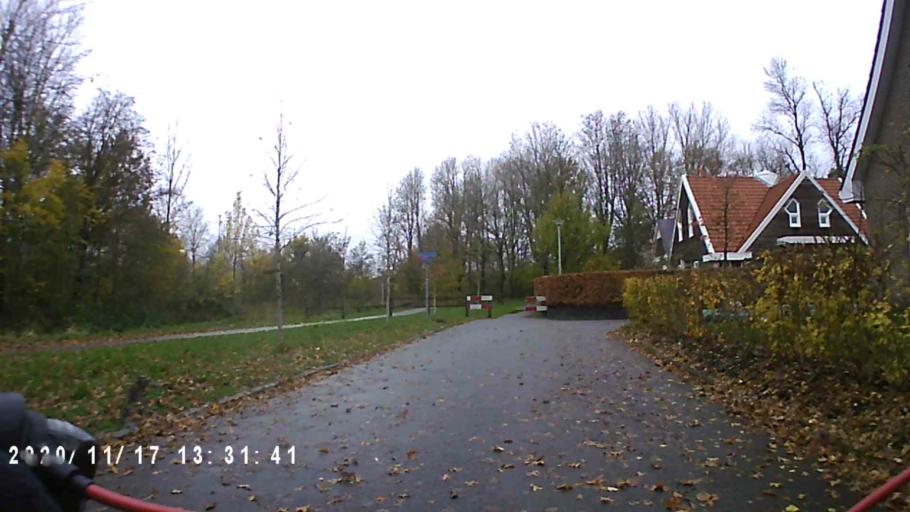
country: NL
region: Groningen
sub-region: Gemeente Zuidhorn
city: Zuidhorn
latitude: 53.2508
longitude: 6.3943
